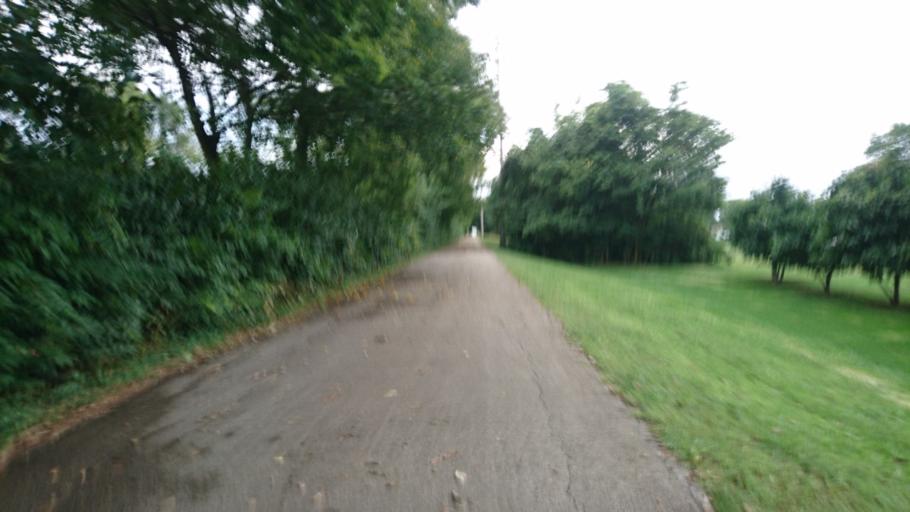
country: US
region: Illinois
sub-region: Sangamon County
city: Chatham
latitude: 39.6798
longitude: -89.7010
